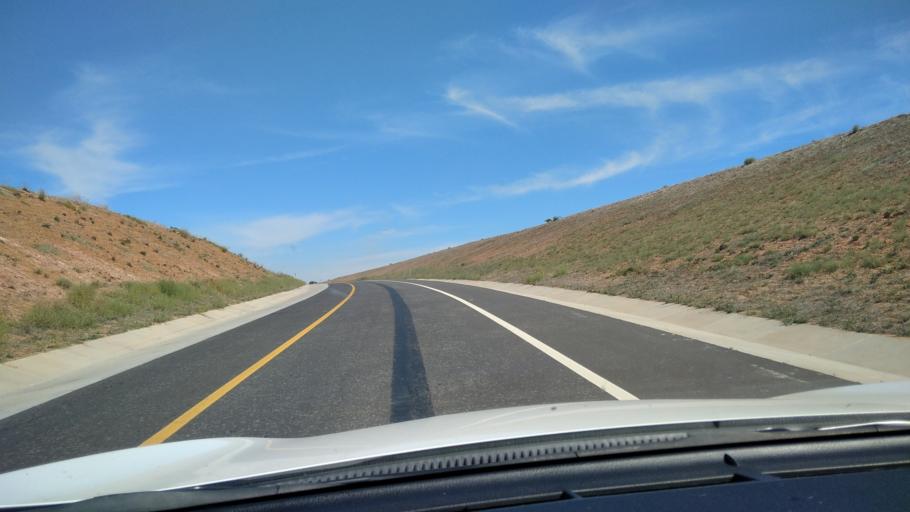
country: ZA
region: Western Cape
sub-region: West Coast District Municipality
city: Malmesbury
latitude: -33.4151
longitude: 18.7142
